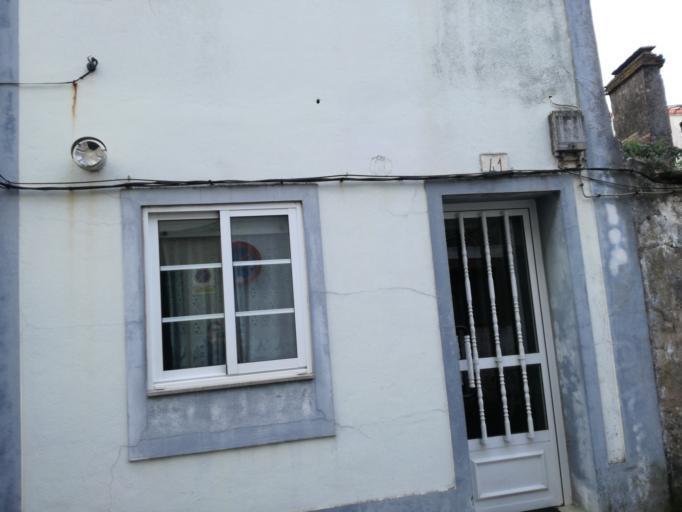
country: ES
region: Galicia
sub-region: Provincia da Coruna
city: Santiago de Compostela
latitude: 42.8806
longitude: -8.5358
